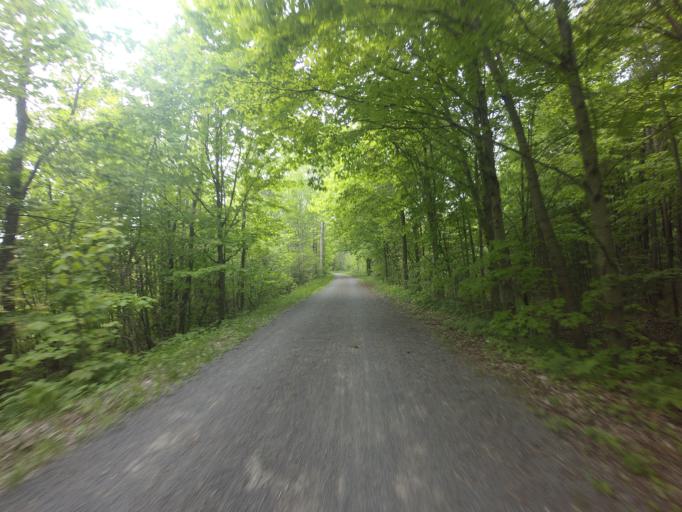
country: CA
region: Ontario
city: Kingston
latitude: 44.3362
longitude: -76.5910
